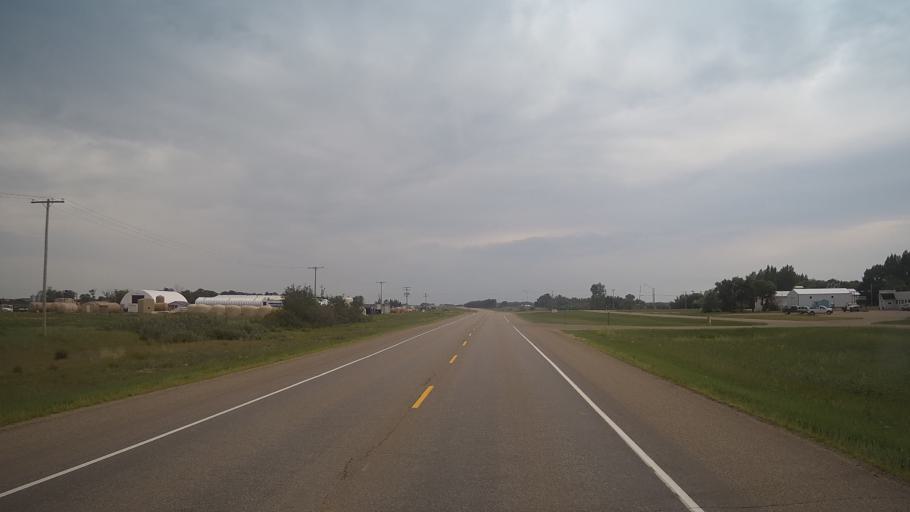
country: CA
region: Saskatchewan
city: Langham
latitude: 52.1289
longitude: -107.2239
